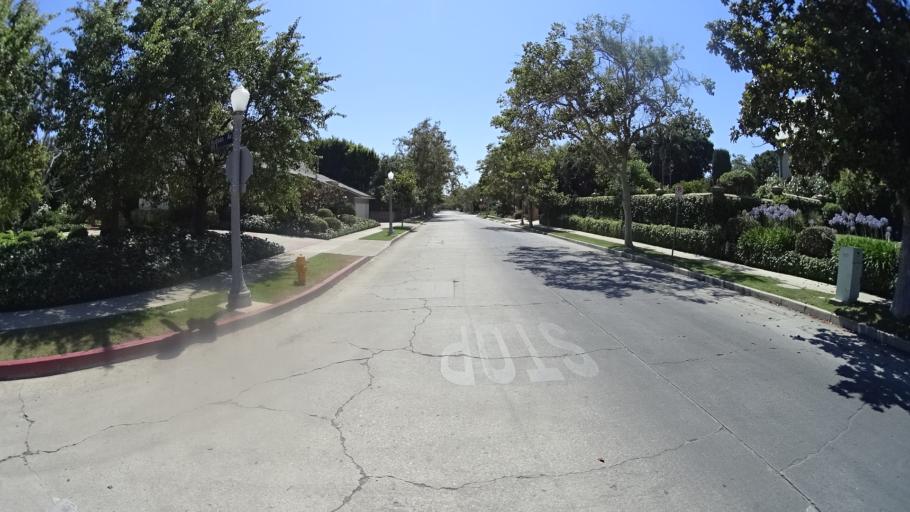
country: US
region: California
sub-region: Los Angeles County
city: Hollywood
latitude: 34.0739
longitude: -118.3330
